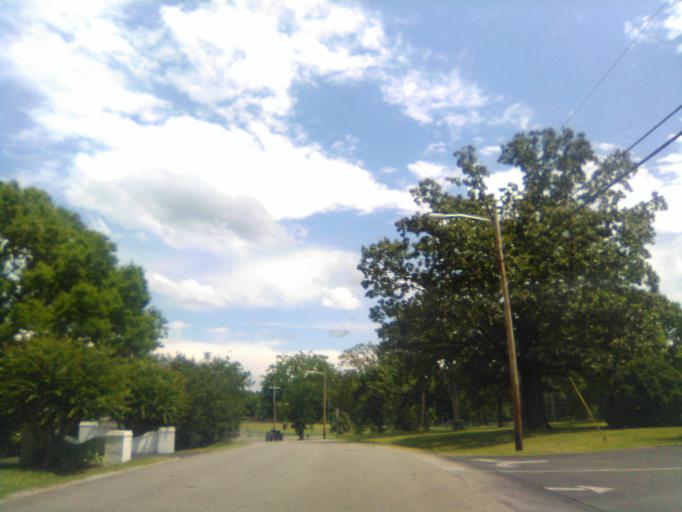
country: US
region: Tennessee
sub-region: Davidson County
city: Belle Meade
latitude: 36.1192
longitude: -86.8769
